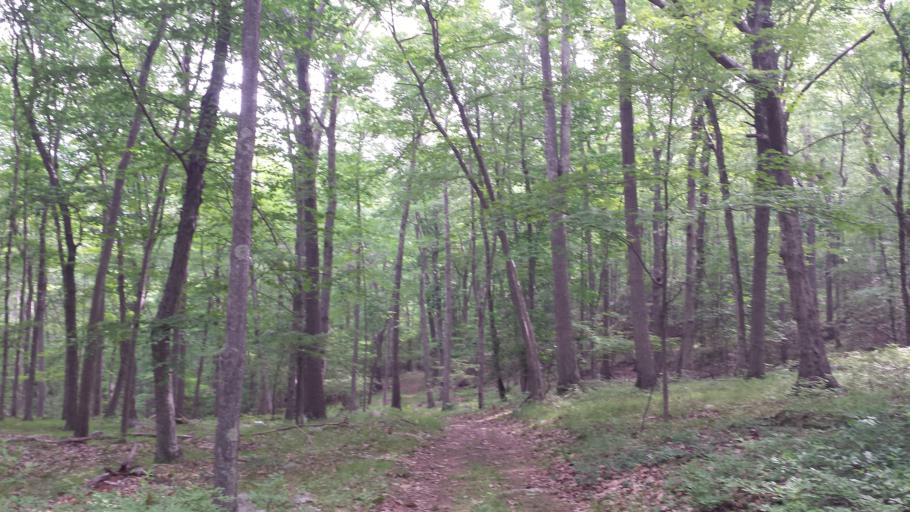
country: US
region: New York
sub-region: Westchester County
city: Pound Ridge
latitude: 41.2319
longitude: -73.5888
